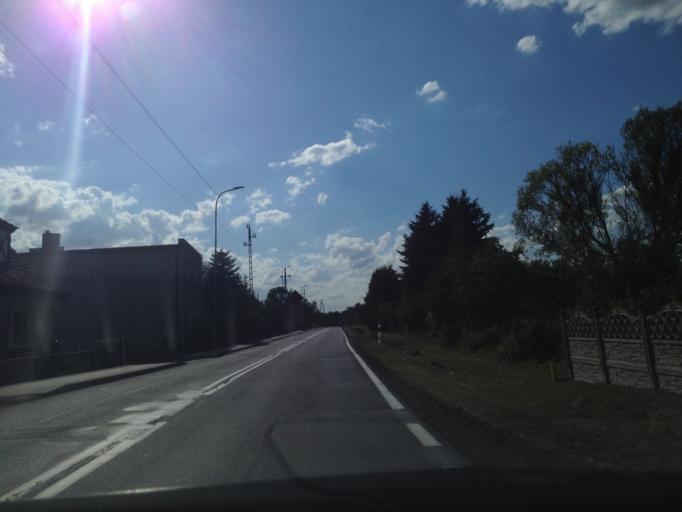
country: PL
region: Lubusz
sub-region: Powiat zarski
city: Lipinki Luzyckie
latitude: 51.6326
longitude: 14.9413
